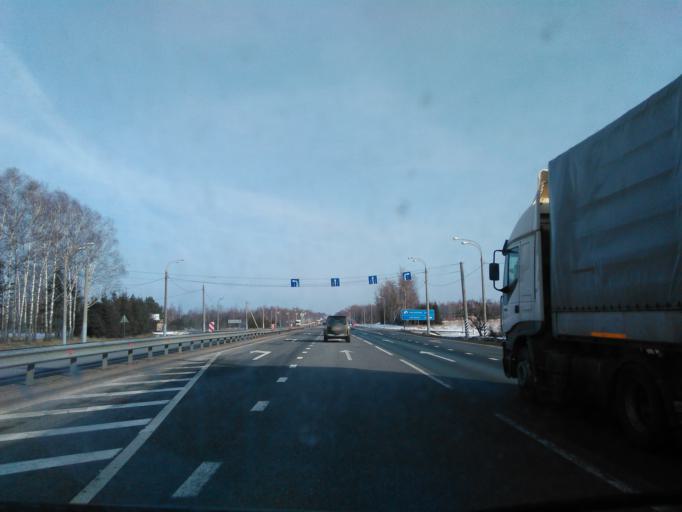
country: RU
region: Smolensk
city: Verkhnedneprovskiy
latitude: 55.1818
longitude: 33.5639
